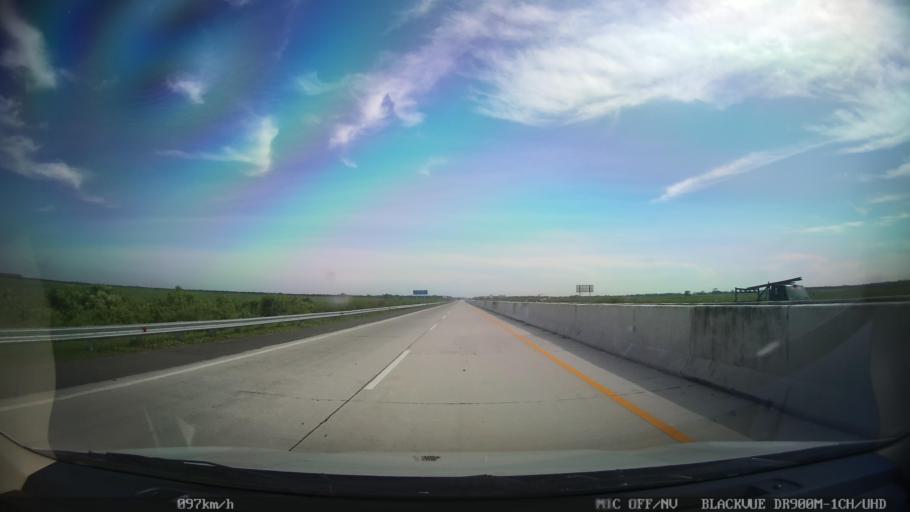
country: ID
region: North Sumatra
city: Binjai
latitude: 3.6765
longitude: 98.5360
